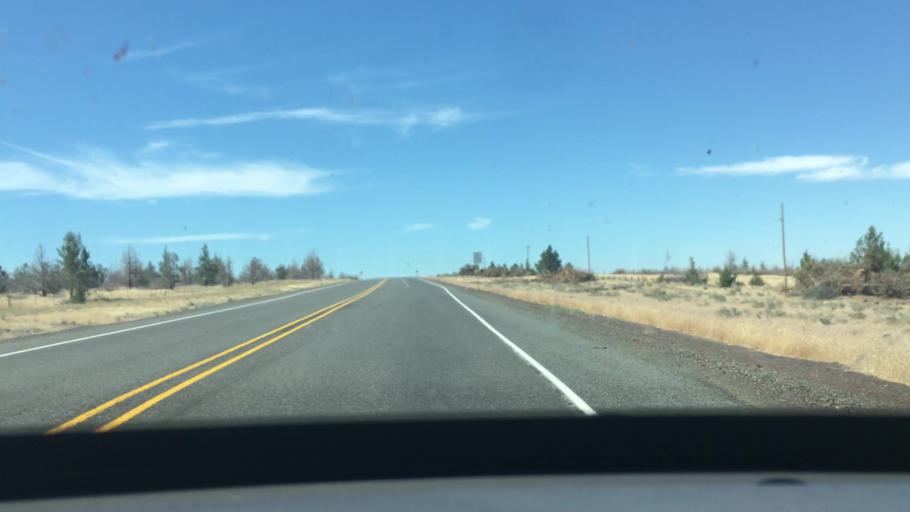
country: US
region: Oregon
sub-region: Jefferson County
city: Madras
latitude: 44.9000
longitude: -120.9373
